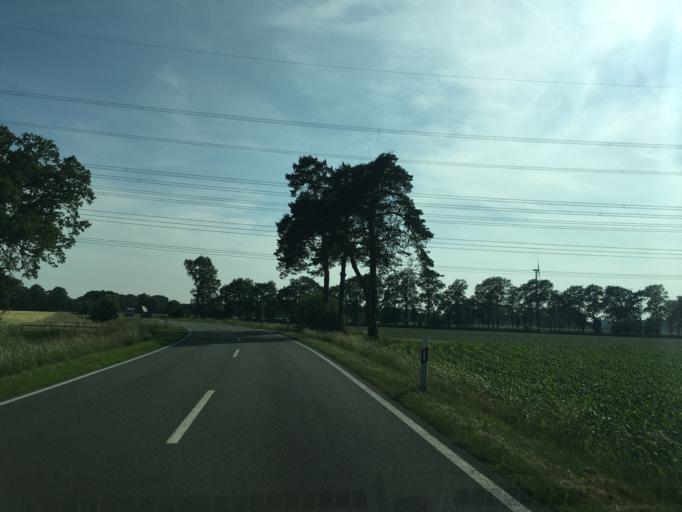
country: DE
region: North Rhine-Westphalia
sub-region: Regierungsbezirk Munster
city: Steinfurt
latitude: 52.1764
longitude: 7.3887
